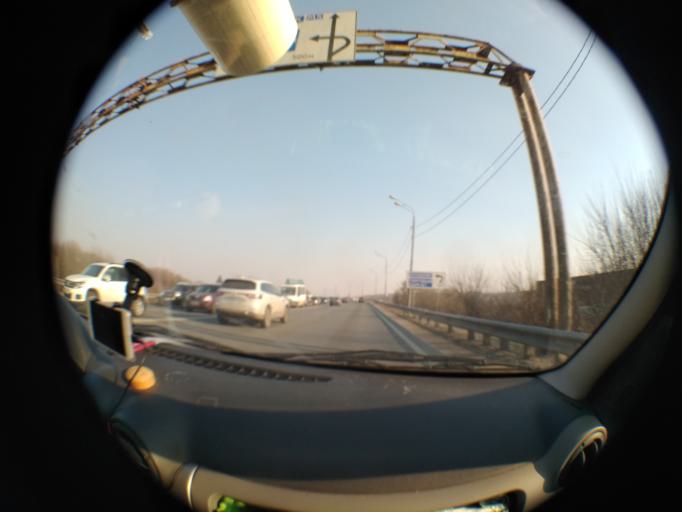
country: RU
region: Moskovskaya
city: Ostrovtsy
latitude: 55.5717
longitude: 38.0305
